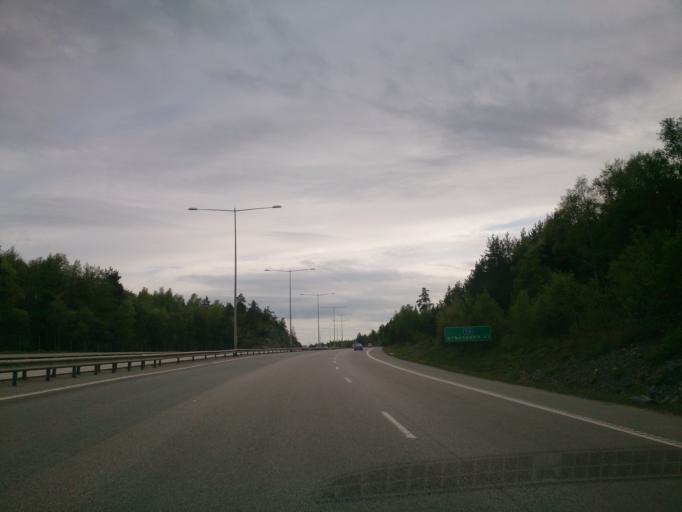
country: SE
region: Stockholm
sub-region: Haninge Kommun
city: Handen
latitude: 59.2147
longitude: 18.1339
